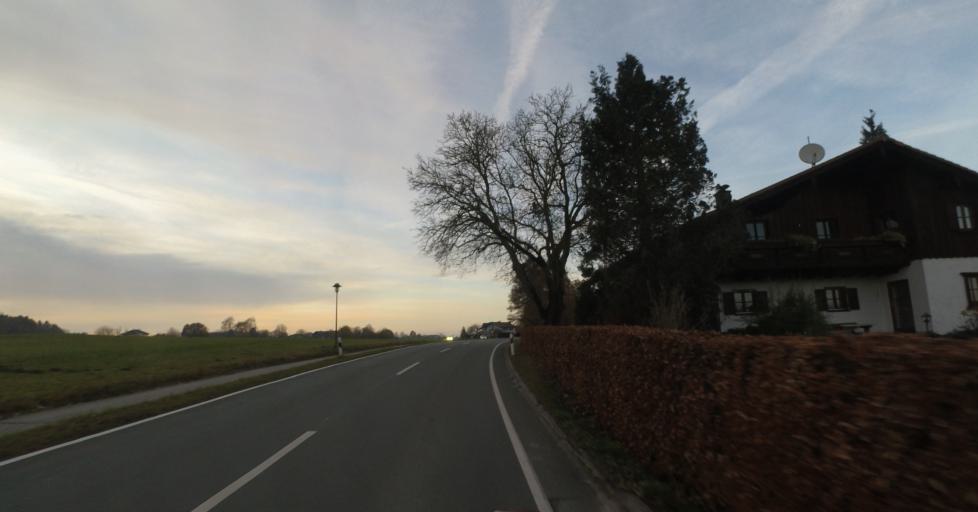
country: DE
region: Bavaria
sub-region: Upper Bavaria
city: Gstadt am Chiemsee
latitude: 47.8941
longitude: 12.3968
